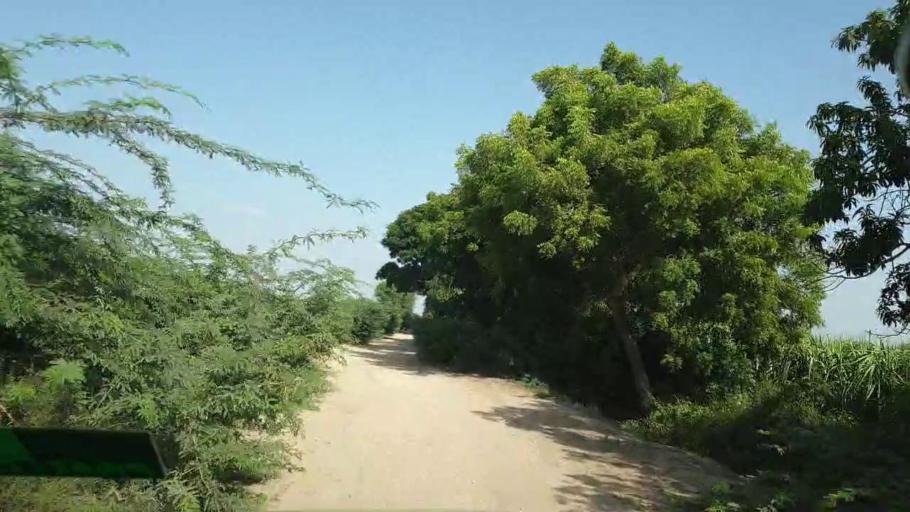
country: PK
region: Sindh
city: Naukot
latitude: 24.7030
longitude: 69.2183
